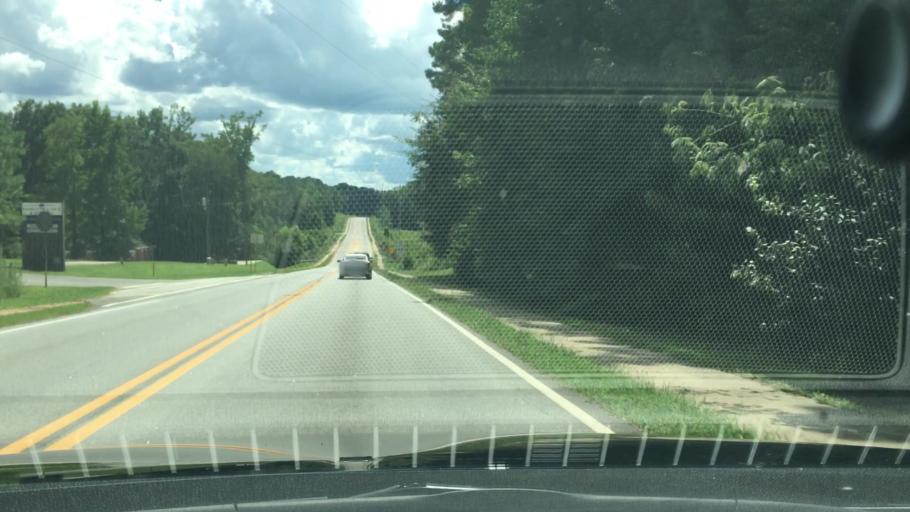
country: US
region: Georgia
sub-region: Putnam County
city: Eatonton
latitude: 33.3333
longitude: -83.3728
